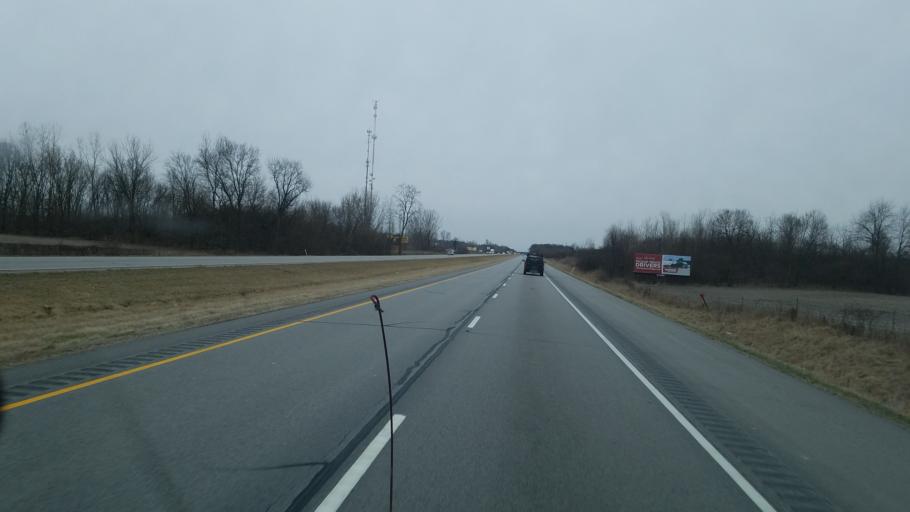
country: US
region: Indiana
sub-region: Marshall County
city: Plymouth
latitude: 41.3261
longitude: -86.2760
